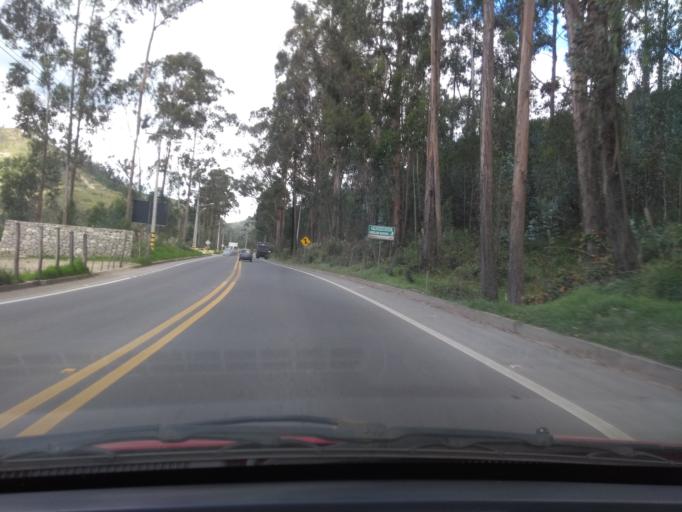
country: EC
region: Azuay
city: Cuenca
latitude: -2.9476
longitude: -79.0470
